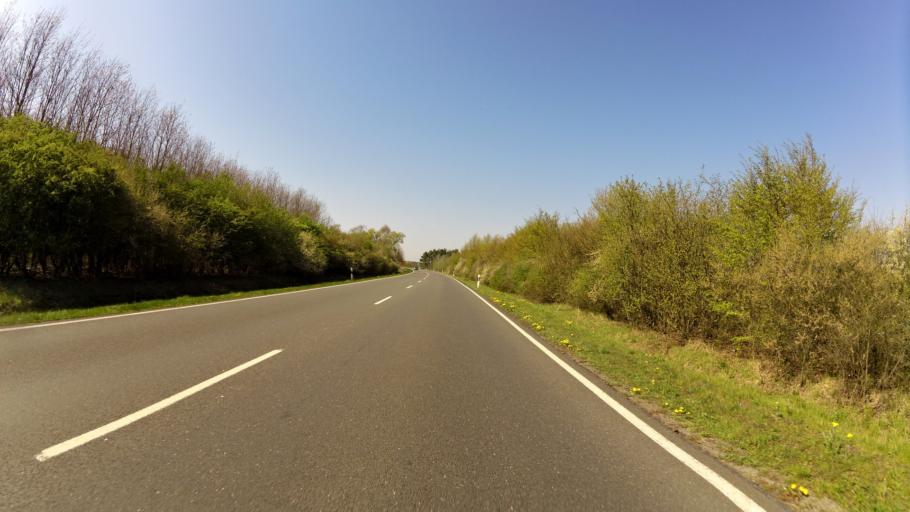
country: DE
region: Saxony-Anhalt
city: Tangermunde
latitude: 52.5719
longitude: 11.9529
